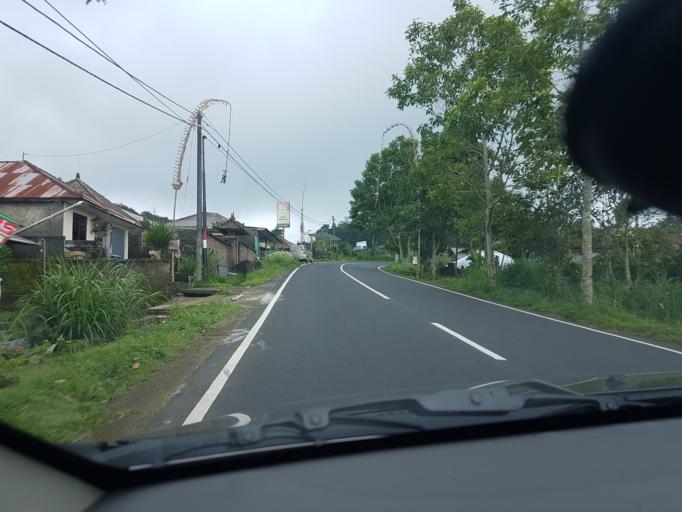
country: ID
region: Bali
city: Banjar Kedisan
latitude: -8.2884
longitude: 115.3619
